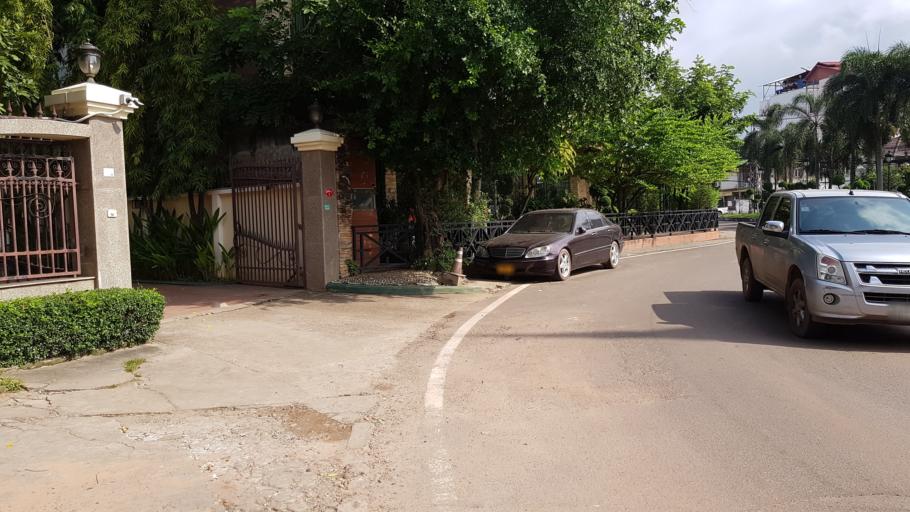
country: LA
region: Vientiane
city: Vientiane
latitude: 17.9661
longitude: 102.6108
